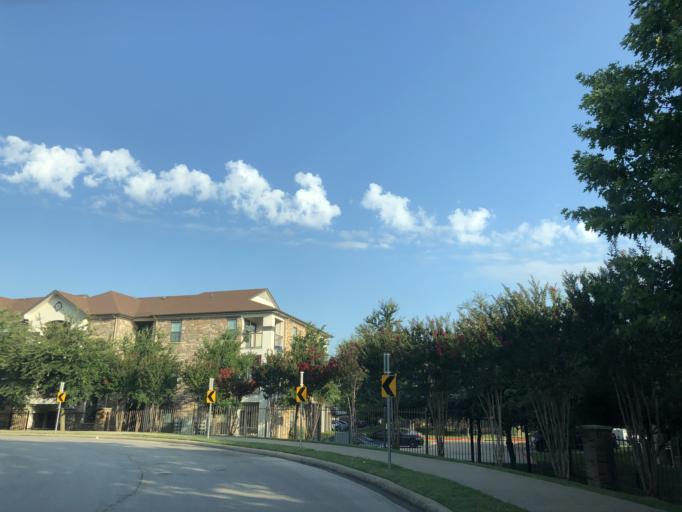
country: US
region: Texas
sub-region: Dallas County
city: Sunnyvale
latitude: 32.8462
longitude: -96.5921
